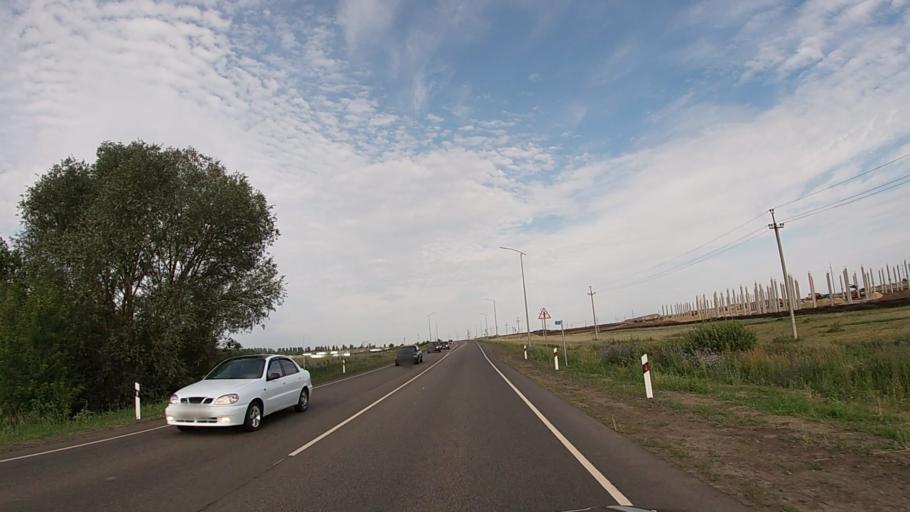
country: RU
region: Belgorod
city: Severnyy
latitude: 50.6673
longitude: 36.5473
